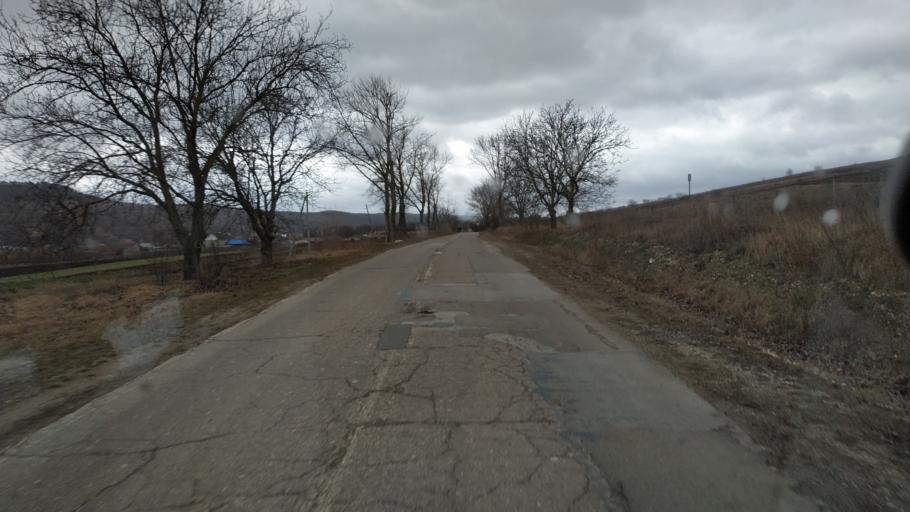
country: MD
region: Calarasi
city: Calarasi
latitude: 47.2428
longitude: 28.2254
